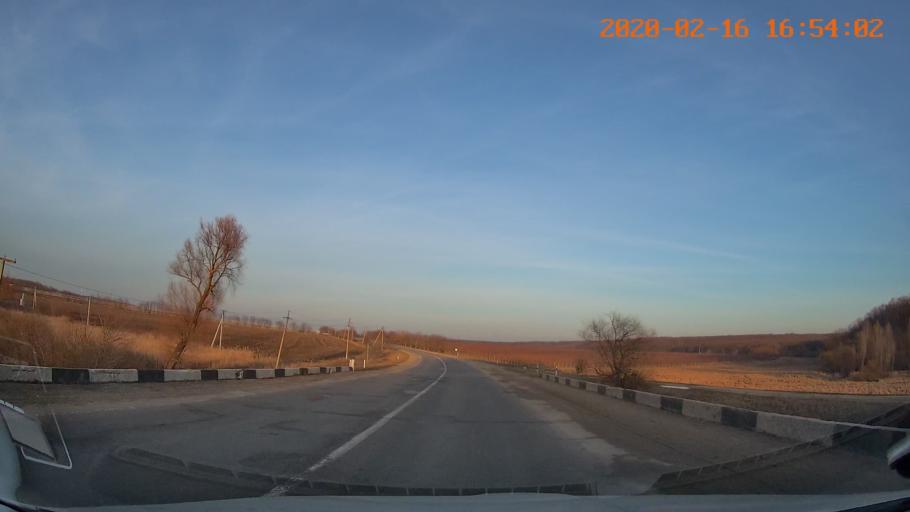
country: MD
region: Briceni
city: Briceni
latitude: 48.3172
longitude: 26.9990
